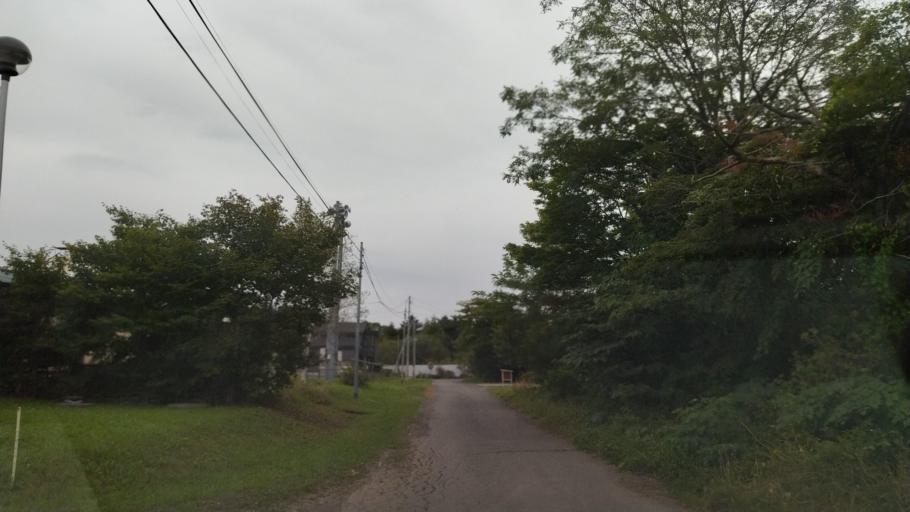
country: JP
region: Hokkaido
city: Otofuke
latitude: 43.2318
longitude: 143.2819
